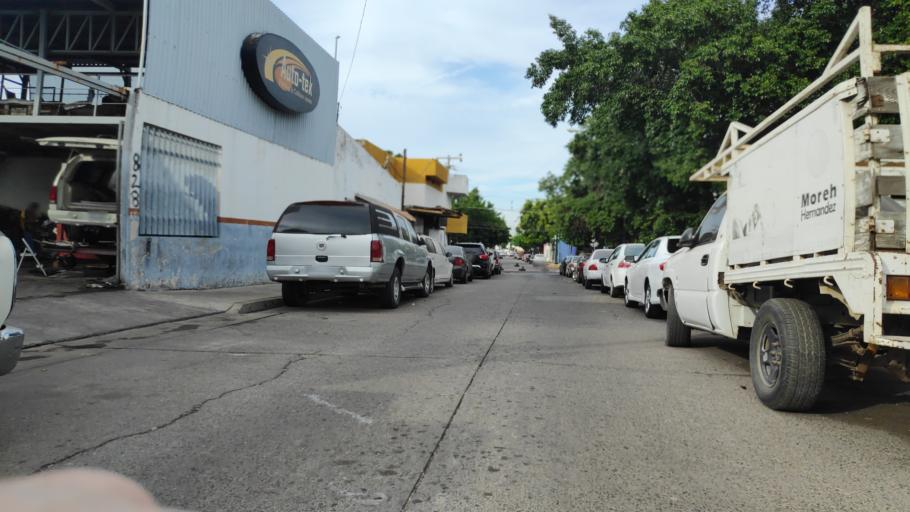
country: MX
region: Sinaloa
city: Culiacan
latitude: 24.7967
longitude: -107.3964
